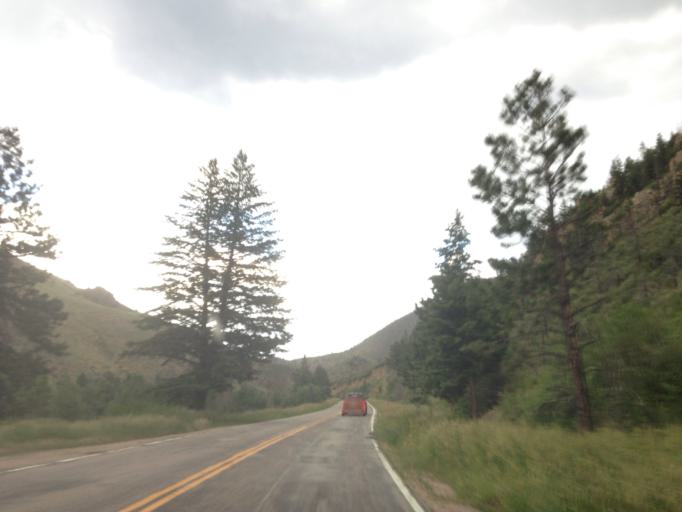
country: US
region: Colorado
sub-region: Larimer County
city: Laporte
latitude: 40.6825
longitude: -105.4021
